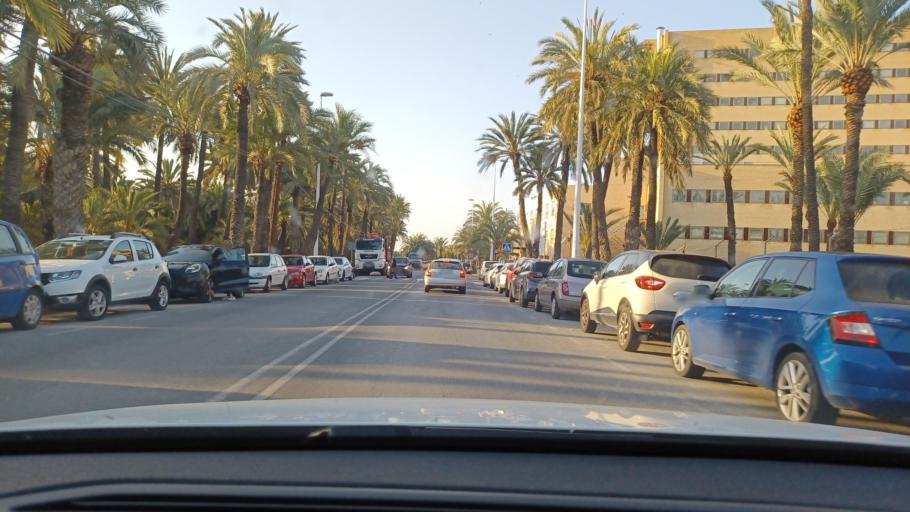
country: ES
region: Valencia
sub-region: Provincia de Alicante
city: Elche
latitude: 38.2611
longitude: -0.6845
